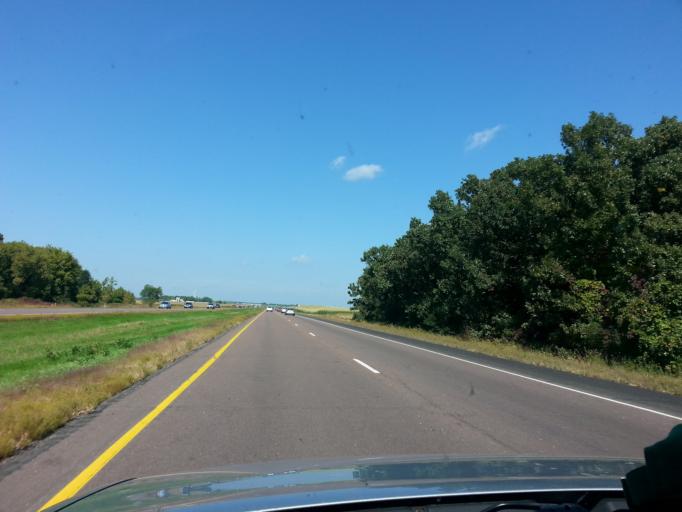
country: US
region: Minnesota
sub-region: Dakota County
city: Rosemount
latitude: 44.6896
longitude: -93.0212
